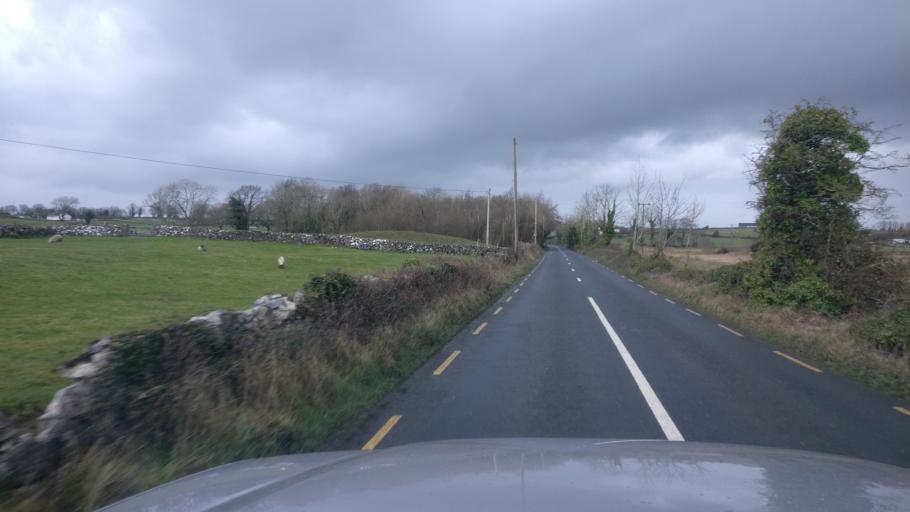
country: IE
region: Connaught
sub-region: County Galway
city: Loughrea
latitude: 53.1723
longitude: -8.6873
